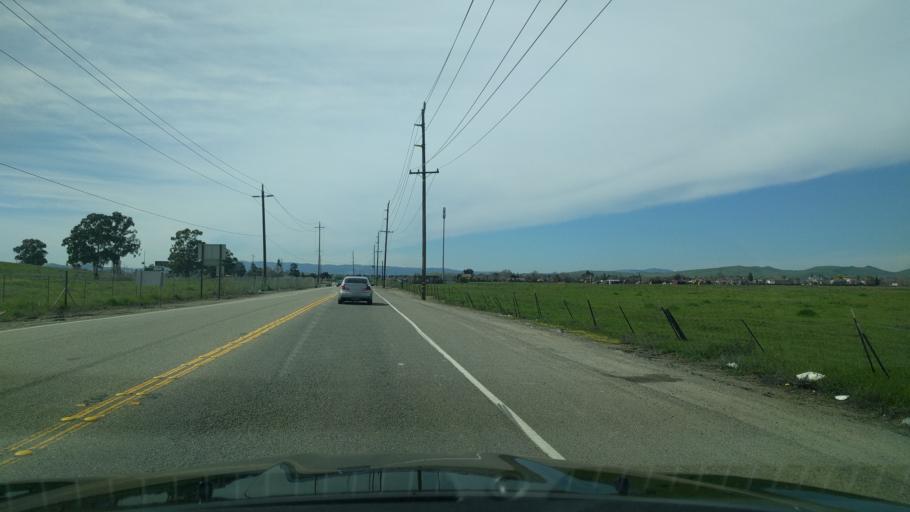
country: US
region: California
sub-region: Alameda County
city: Livermore
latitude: 37.7189
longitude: -121.7019
